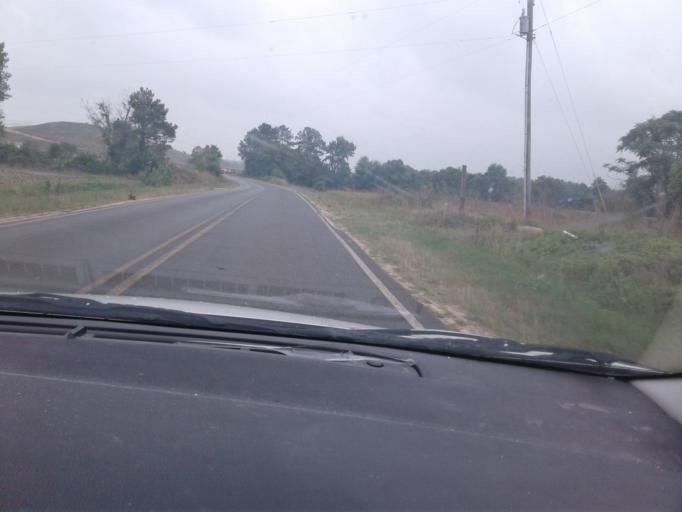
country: US
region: North Carolina
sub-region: Harnett County
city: Coats
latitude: 35.3716
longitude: -78.6480
